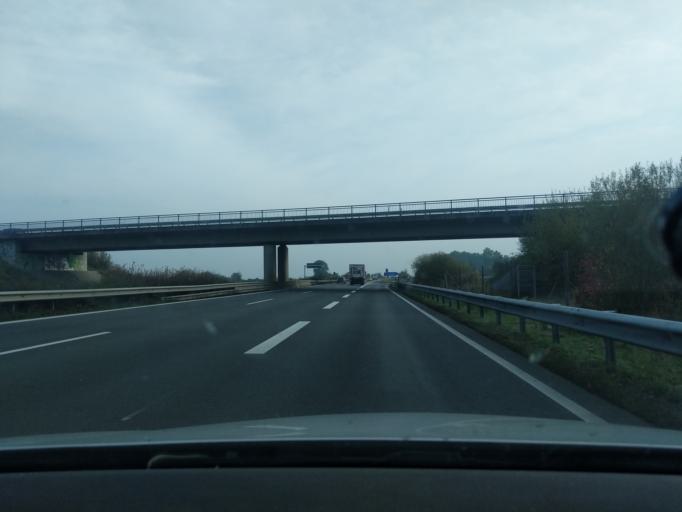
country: DE
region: Lower Saxony
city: Dollern
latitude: 53.5452
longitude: 9.5695
